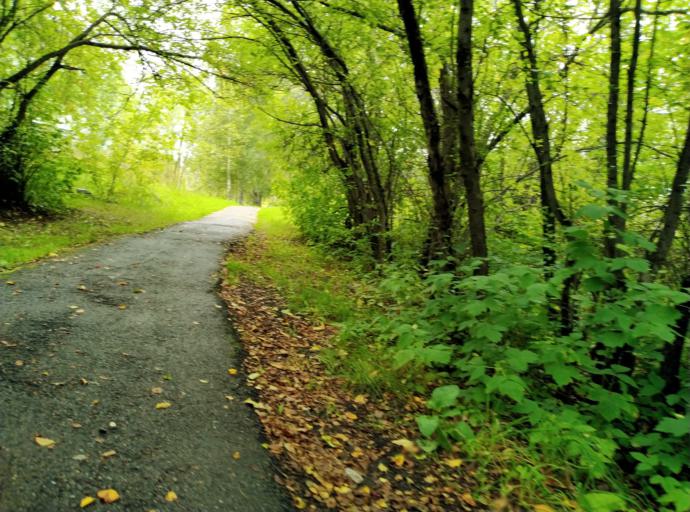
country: RU
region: Krasnoyarskiy
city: Krasnoyarsk
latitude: 55.9881
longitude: 92.7620
